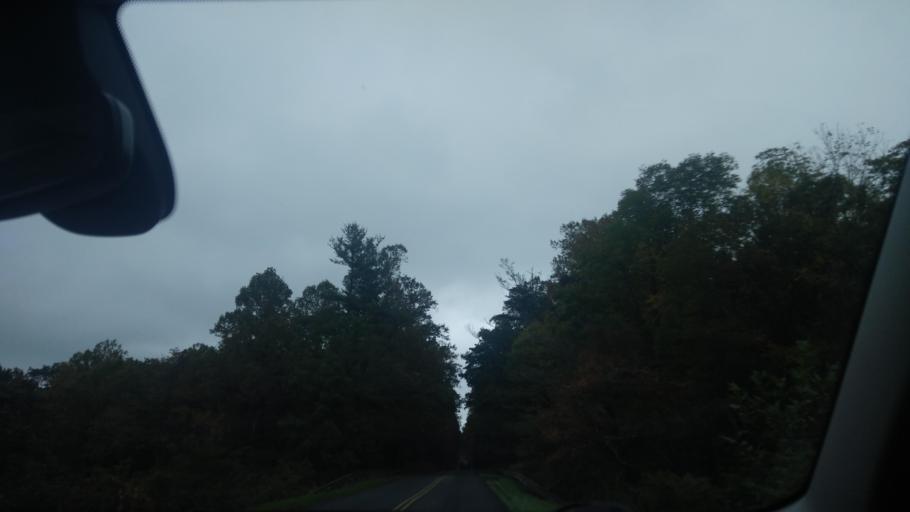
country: US
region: Virginia
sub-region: Carroll County
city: Cana
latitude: 36.6701
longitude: -80.6305
